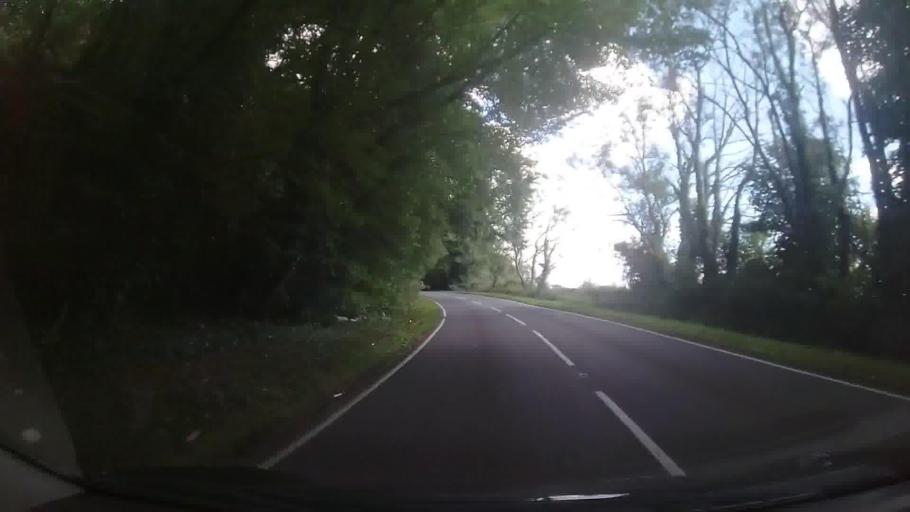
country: GB
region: Wales
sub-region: Pembrokeshire
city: Pembroke
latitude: 51.6776
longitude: -4.8975
